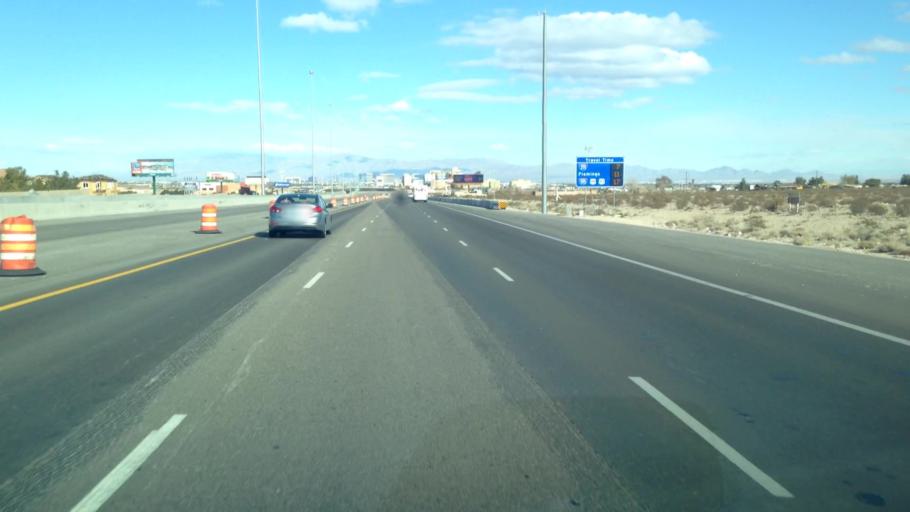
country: US
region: Nevada
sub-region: Clark County
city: Enterprise
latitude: 35.9759
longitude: -115.1811
